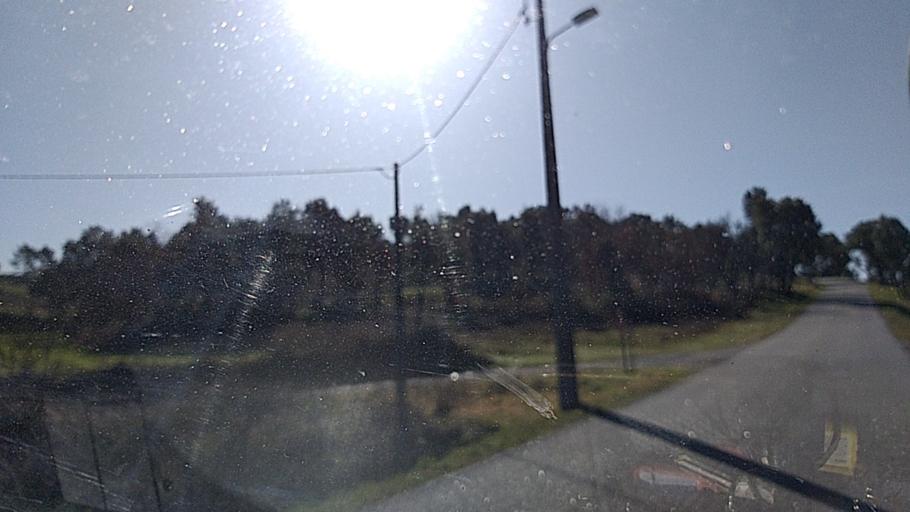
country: PT
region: Guarda
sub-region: Celorico da Beira
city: Celorico da Beira
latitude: 40.6954
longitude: -7.4499
